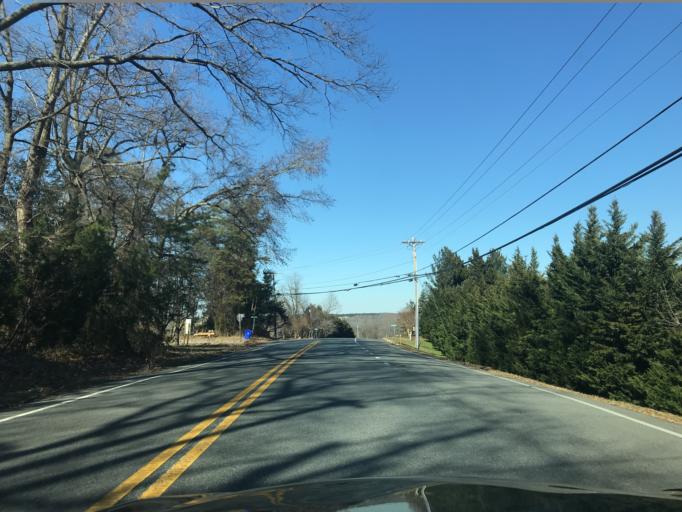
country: US
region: Maryland
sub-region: Charles County
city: Bennsville
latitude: 38.6354
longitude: -77.0153
